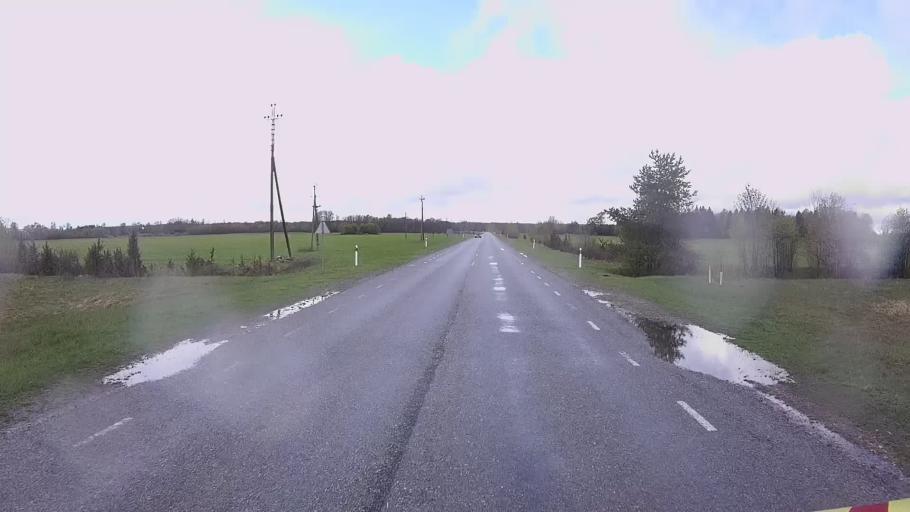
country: EE
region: Hiiumaa
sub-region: Kaerdla linn
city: Kardla
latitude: 58.8297
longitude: 22.7654
